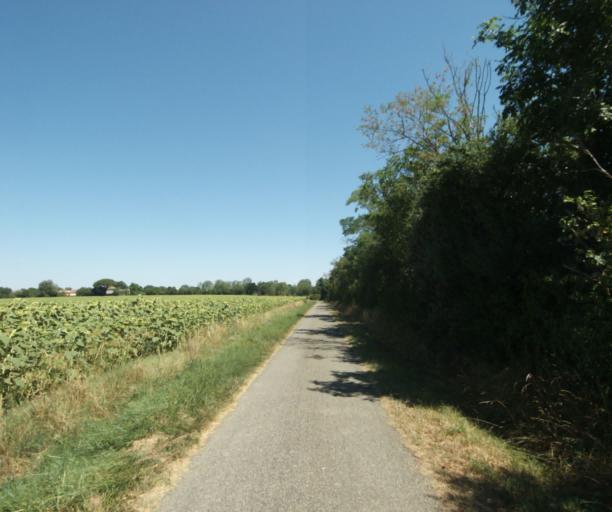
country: FR
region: Midi-Pyrenees
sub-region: Departement de la Haute-Garonne
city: Saint-Felix-Lauragais
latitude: 43.4590
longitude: 1.9344
